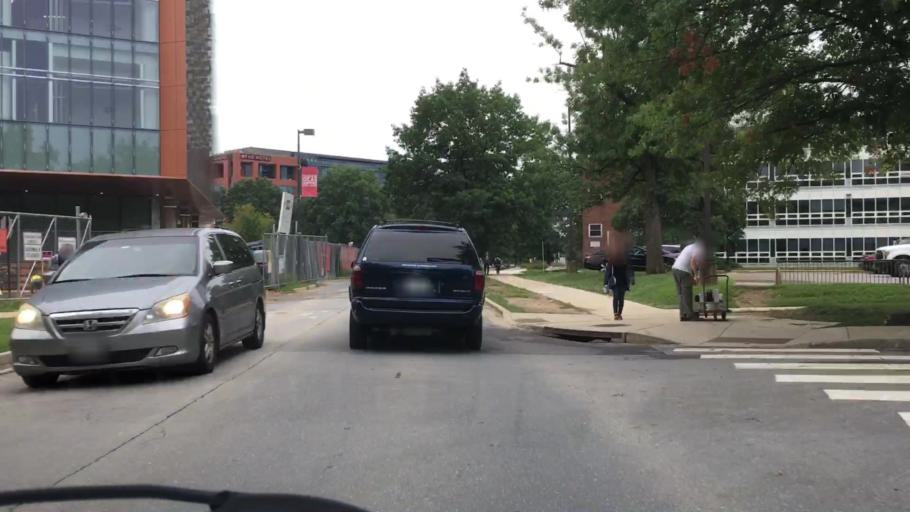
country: US
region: Maryland
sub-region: Prince George's County
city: College Park
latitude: 38.9897
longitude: -76.9372
